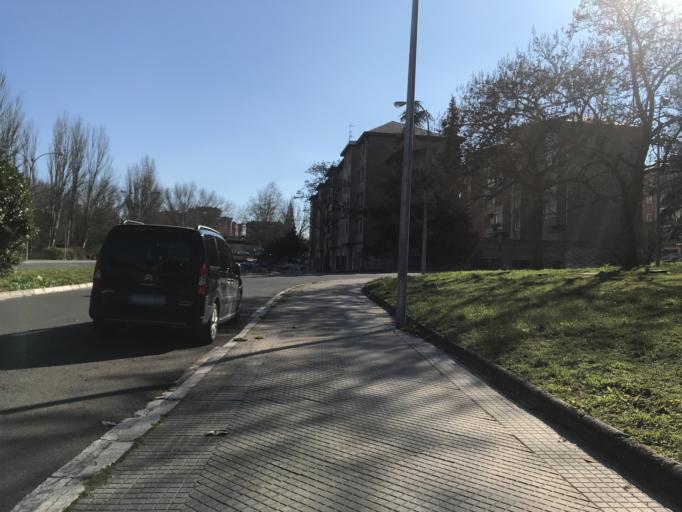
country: ES
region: Basque Country
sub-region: Provincia de Alava
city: Gasteiz / Vitoria
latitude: 42.8511
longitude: -2.6579
